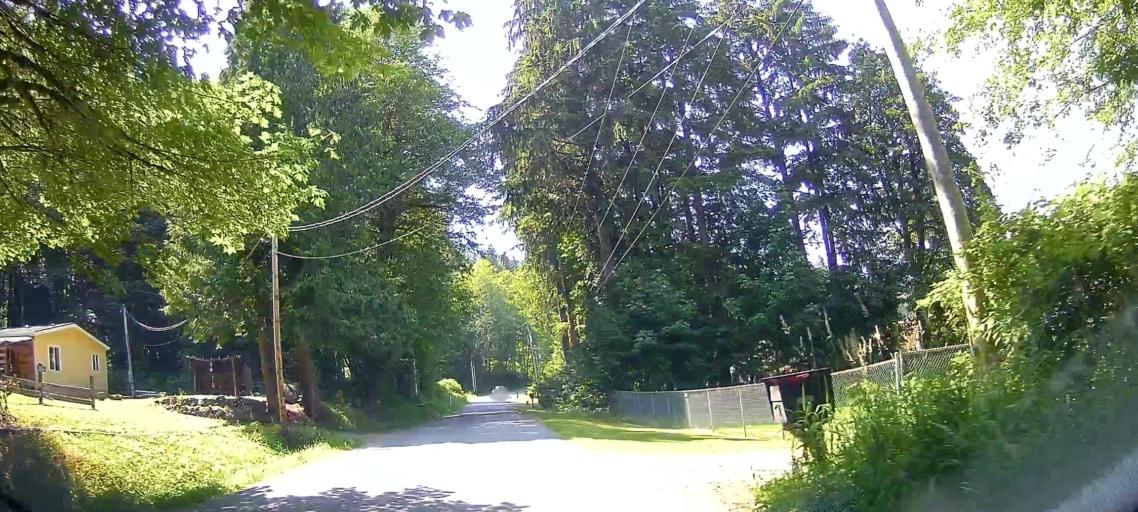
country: US
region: Washington
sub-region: Snohomish County
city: Arlington Heights
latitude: 48.3179
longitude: -122.0241
